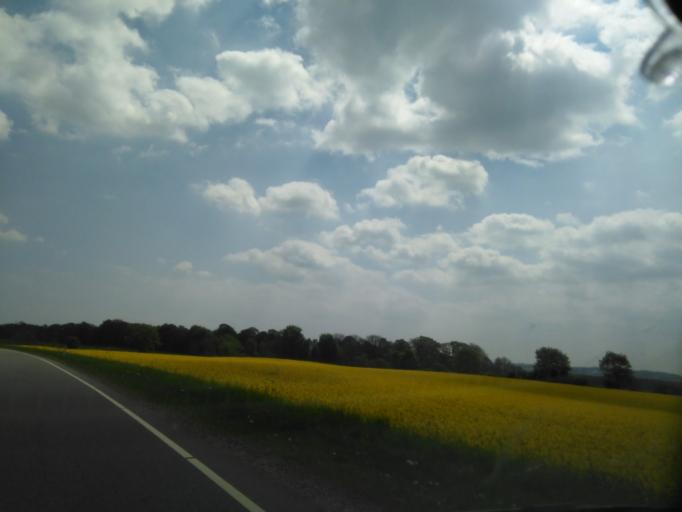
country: DK
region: Central Jutland
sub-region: Skanderborg Kommune
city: Stilling
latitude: 56.0029
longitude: 10.0006
